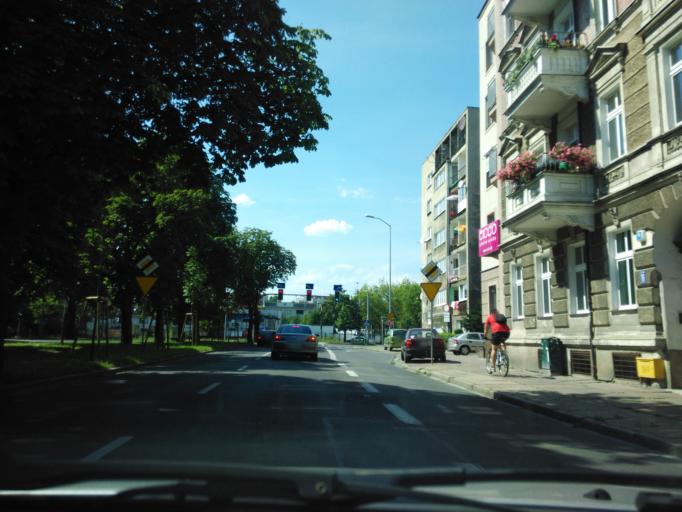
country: PL
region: West Pomeranian Voivodeship
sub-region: Szczecin
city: Szczecin
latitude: 53.4223
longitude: 14.5366
